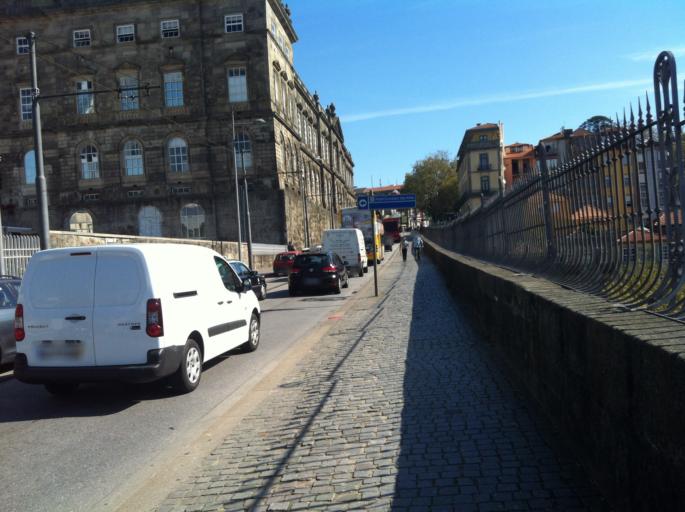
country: PT
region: Porto
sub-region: Porto
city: Porto
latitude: 41.1461
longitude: -8.6194
